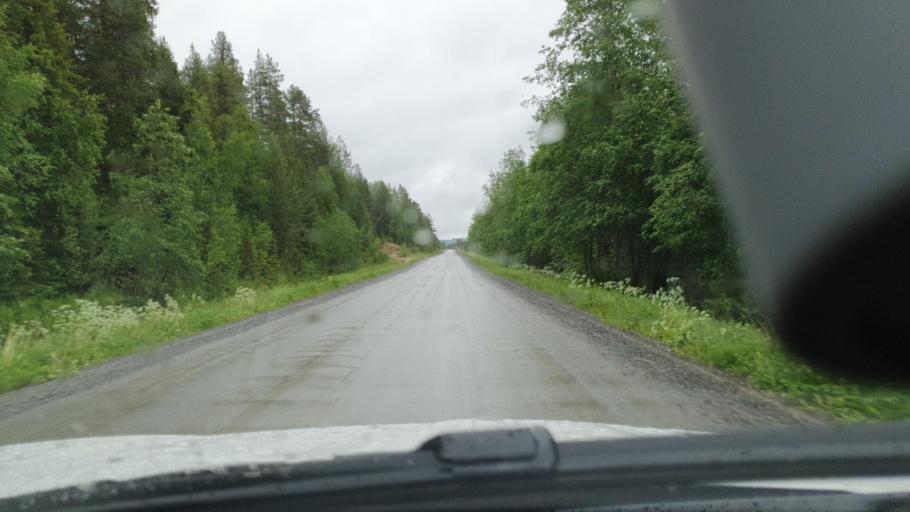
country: SE
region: Vaesterbotten
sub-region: Skelleftea Kommun
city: Burtraesk
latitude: 64.3761
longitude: 20.3572
